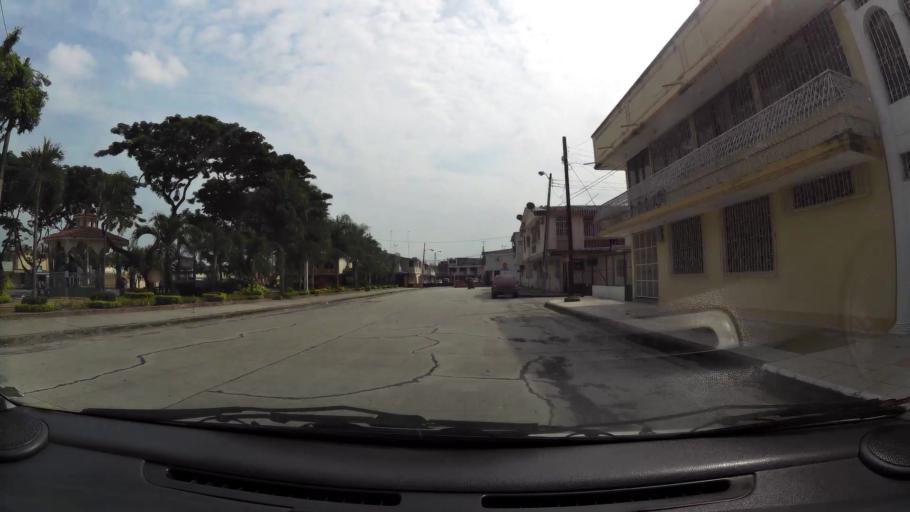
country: EC
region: Guayas
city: Guayaquil
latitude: -2.2427
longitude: -79.9016
